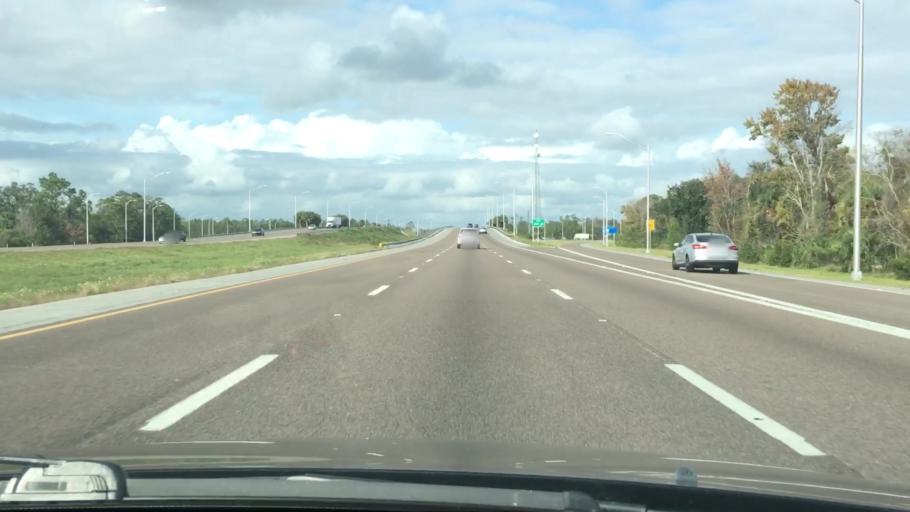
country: US
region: Florida
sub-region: Volusia County
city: Edgewater
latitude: 28.9469
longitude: -80.9486
